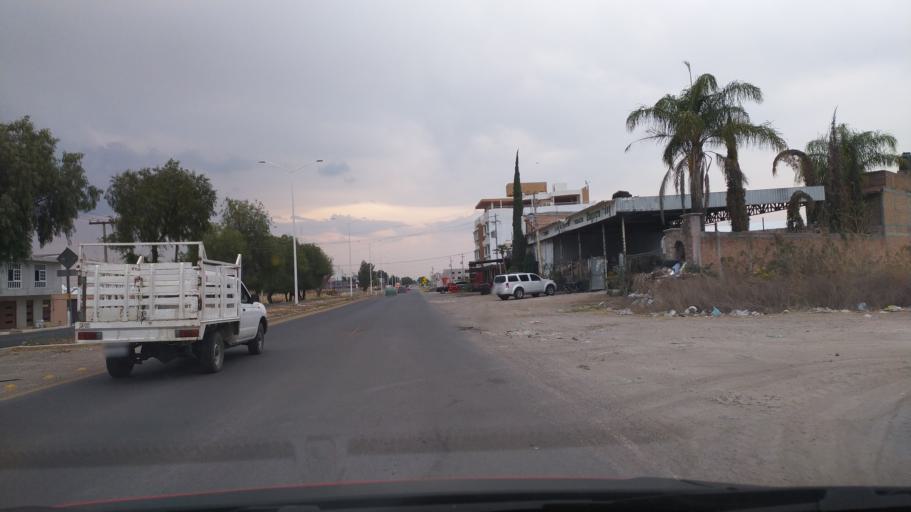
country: MX
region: Guanajuato
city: Ciudad Manuel Doblado
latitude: 20.7281
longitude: -101.9402
